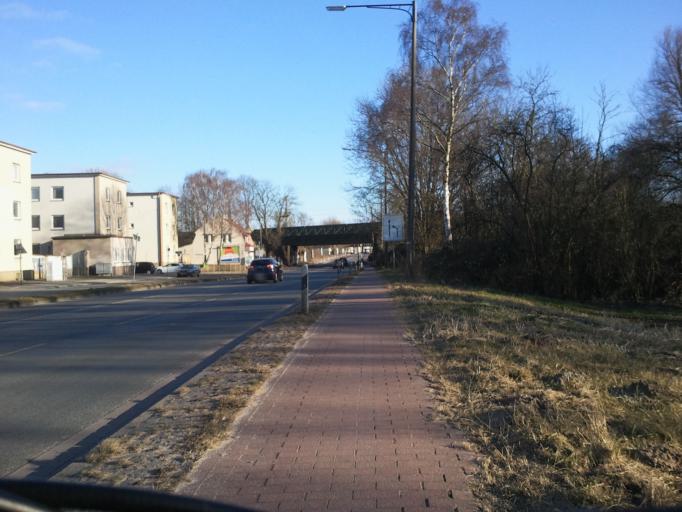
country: DE
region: Bremen
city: Bremen
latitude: 53.0708
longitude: 8.7740
